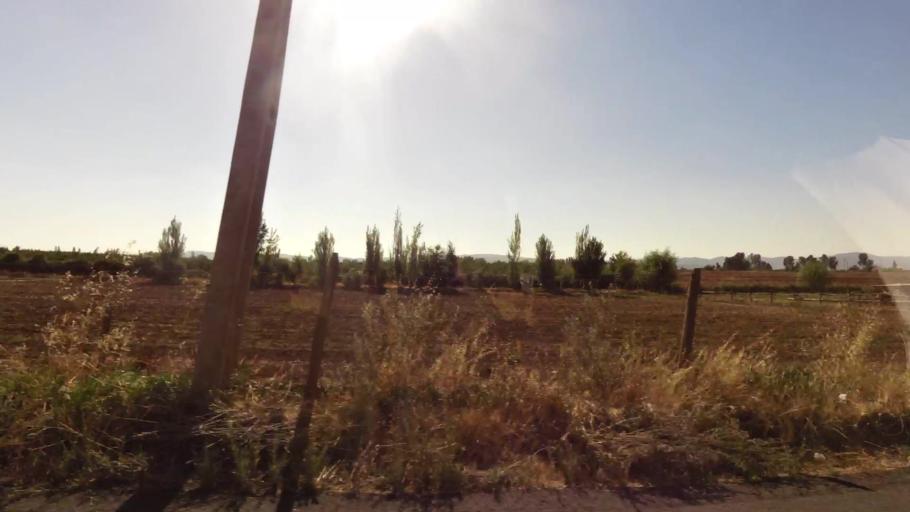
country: CL
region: Maule
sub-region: Provincia de Talca
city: Talca
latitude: -35.4111
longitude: -71.5924
